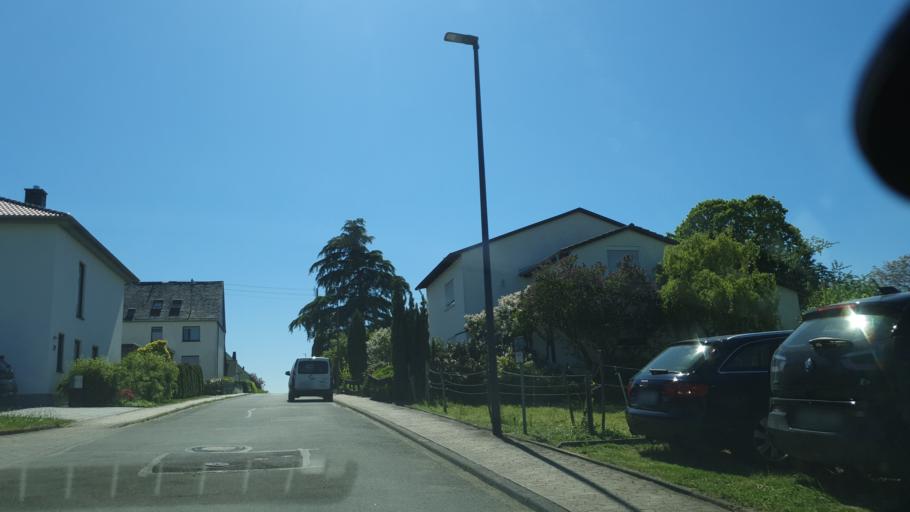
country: DE
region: Rheinland-Pfalz
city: Frucht
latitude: 50.3148
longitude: 7.6758
